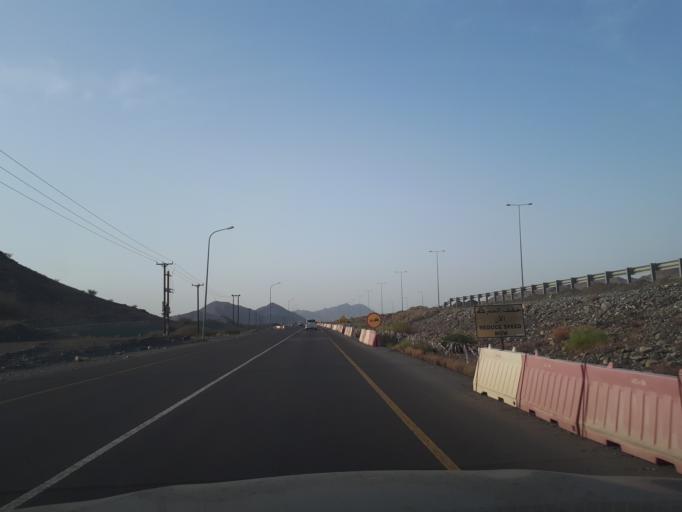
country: OM
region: Muhafazat ad Dakhiliyah
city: Sufalat Sama'il
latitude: 23.2863
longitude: 58.1084
